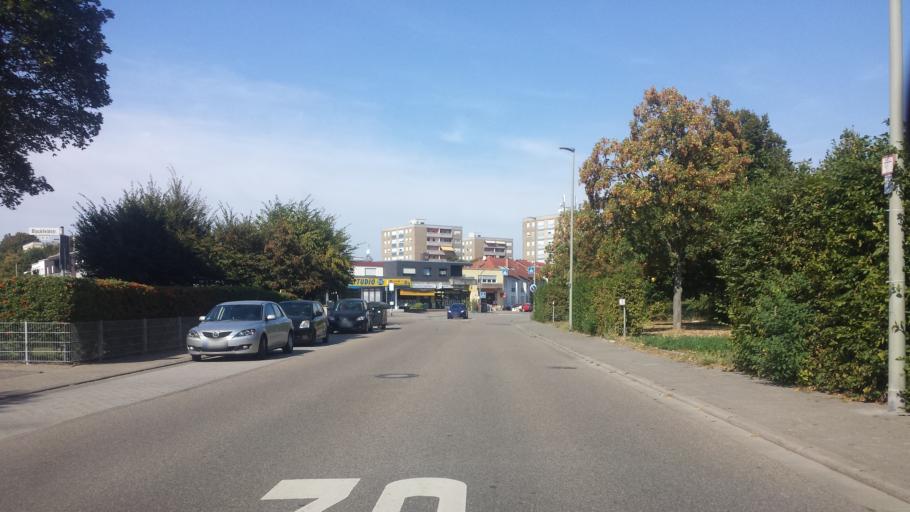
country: DE
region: Rheinland-Pfalz
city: Mutterstadt
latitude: 49.4381
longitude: 8.3518
